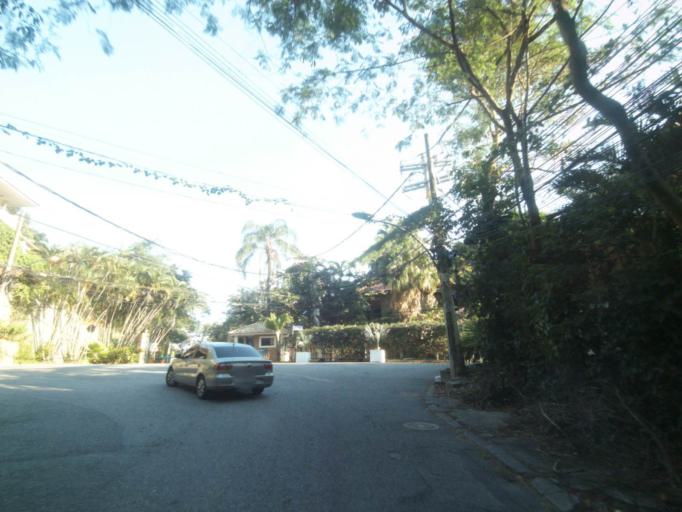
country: BR
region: Rio de Janeiro
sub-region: Rio De Janeiro
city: Rio de Janeiro
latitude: -23.0093
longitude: -43.2906
